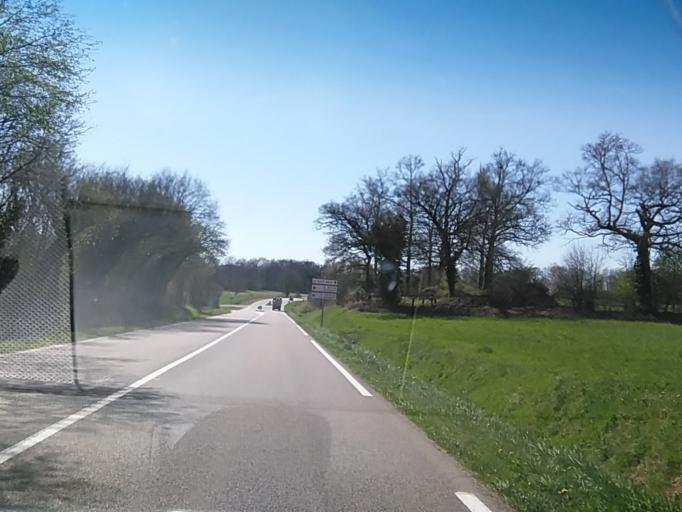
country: FR
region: Lower Normandy
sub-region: Departement de l'Orne
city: Magny-le-Desert
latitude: 48.5826
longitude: -0.2531
